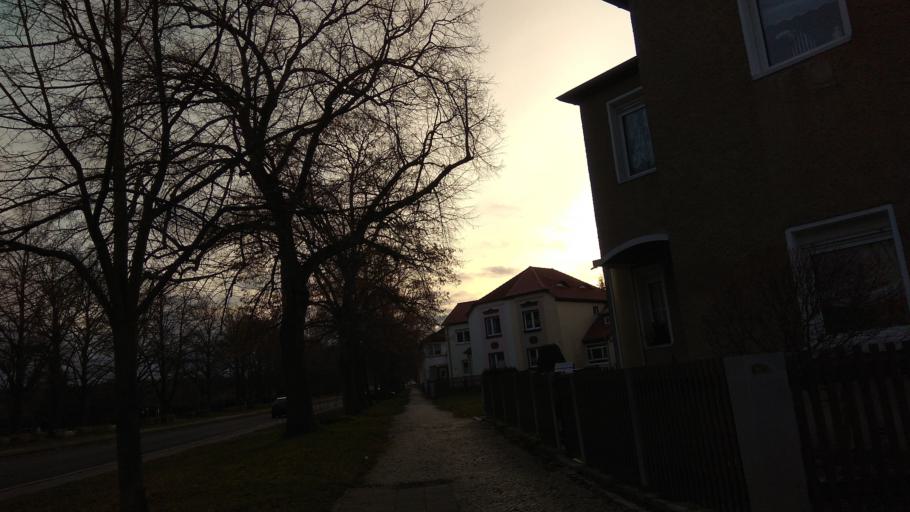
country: DE
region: Saxony-Anhalt
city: Halberstadt
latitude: 51.8762
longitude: 11.0530
